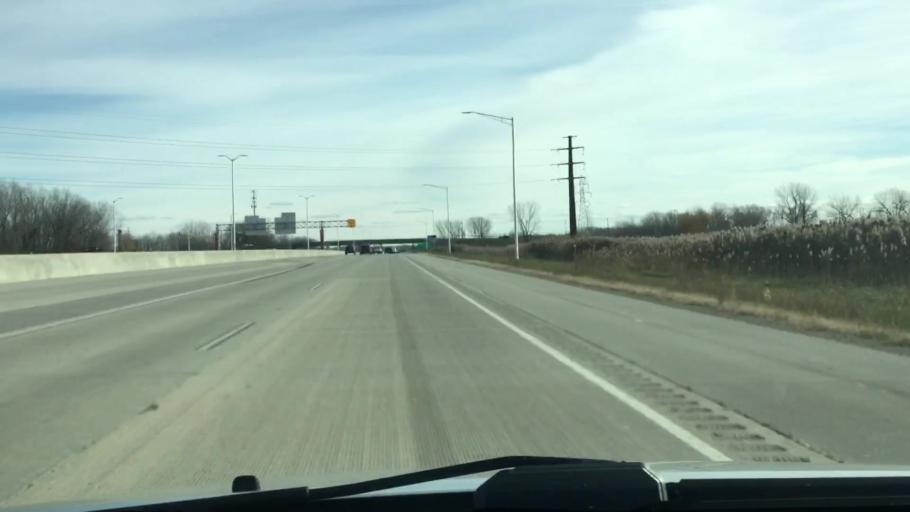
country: US
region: Wisconsin
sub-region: Brown County
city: Howard
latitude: 44.5553
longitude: -88.0465
